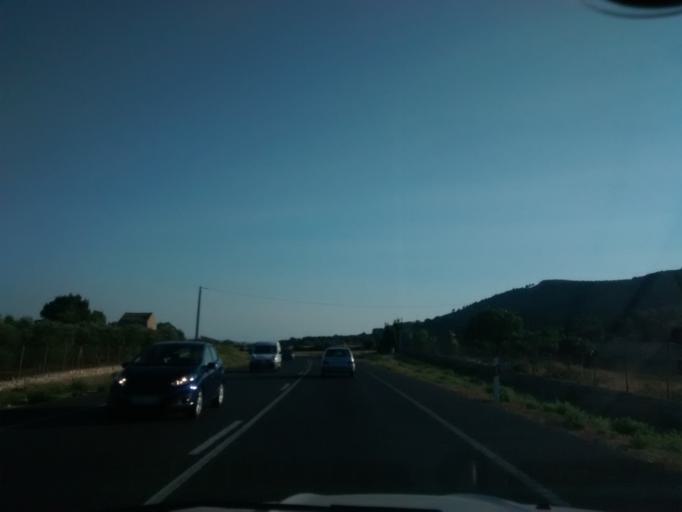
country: ES
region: Balearic Islands
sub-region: Illes Balears
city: Alcudia
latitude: 39.8289
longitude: 3.0624
